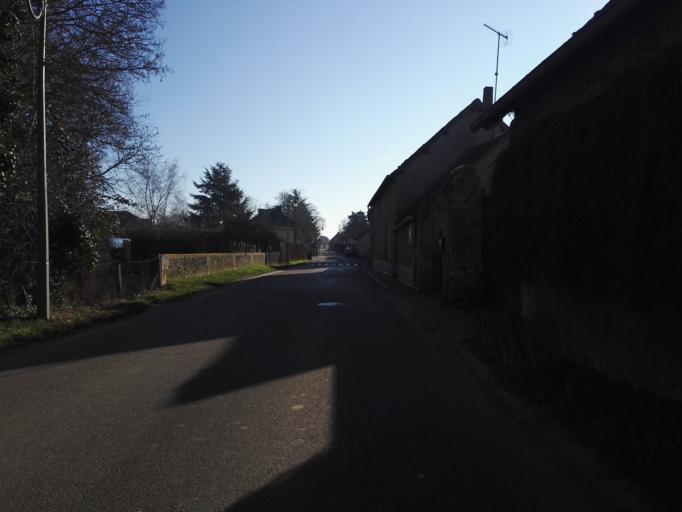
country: FR
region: Haute-Normandie
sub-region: Departement de l'Eure
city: Pacy-sur-Eure
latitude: 49.0081
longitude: 1.4193
